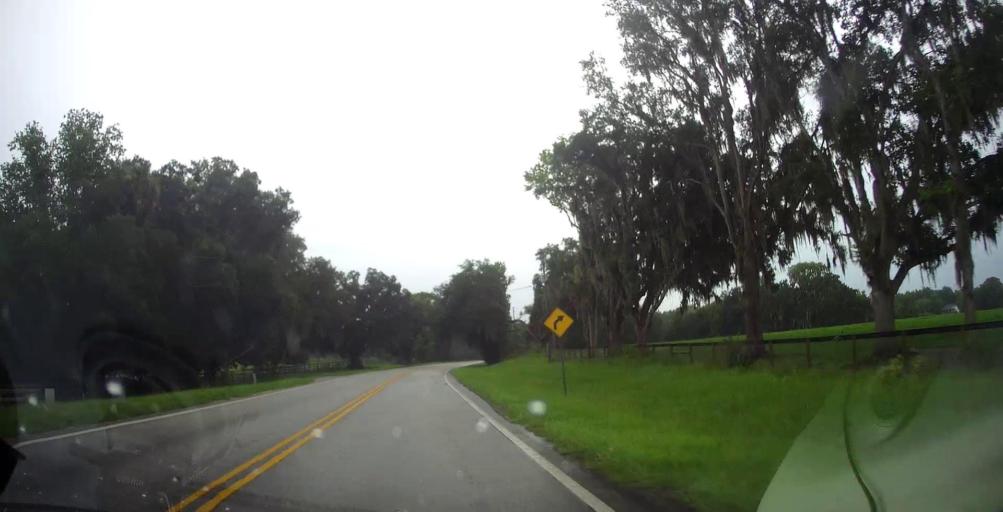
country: US
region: Florida
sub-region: Marion County
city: Citra
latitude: 29.3997
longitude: -82.2479
